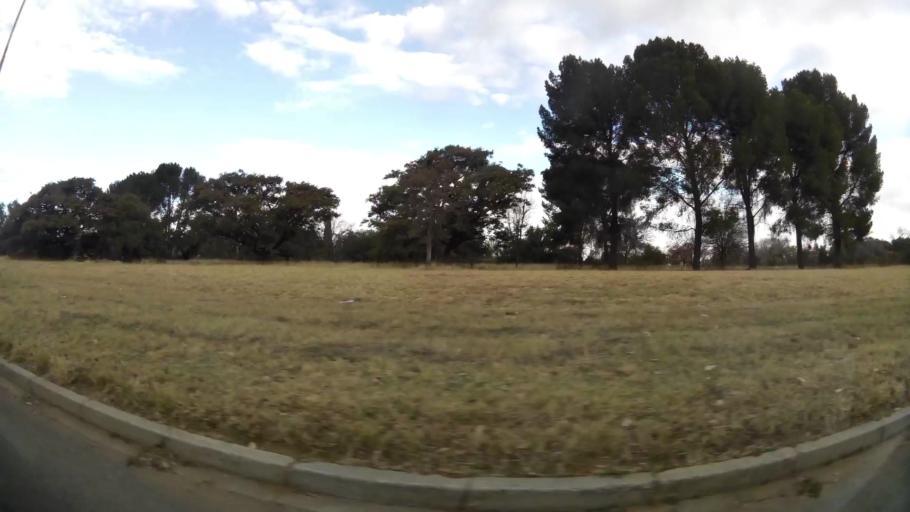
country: ZA
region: Orange Free State
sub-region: Lejweleputswa District Municipality
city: Welkom
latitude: -27.9961
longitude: 26.7149
